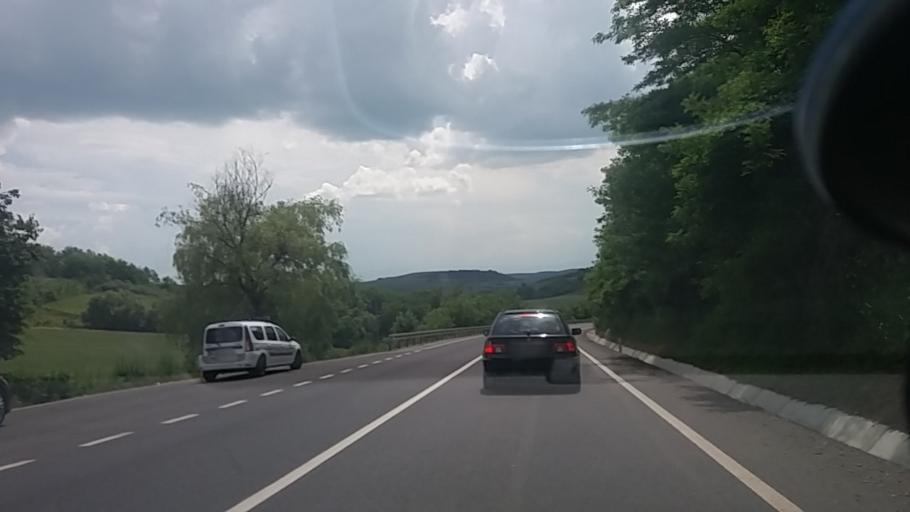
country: RO
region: Sibiu
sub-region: Comuna Slimnic
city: Slimnic
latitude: 45.9361
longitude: 24.1723
